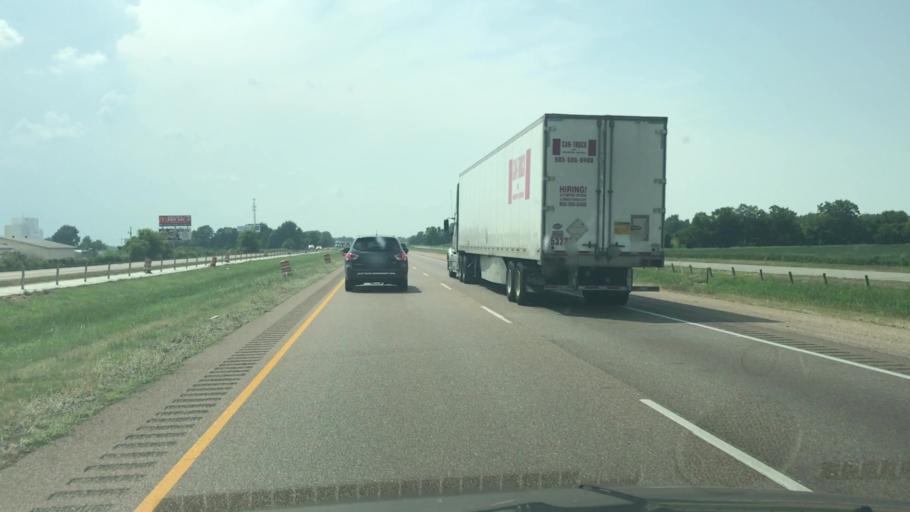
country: US
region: Arkansas
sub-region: Crittenden County
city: West Memphis
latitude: 35.1492
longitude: -90.3484
